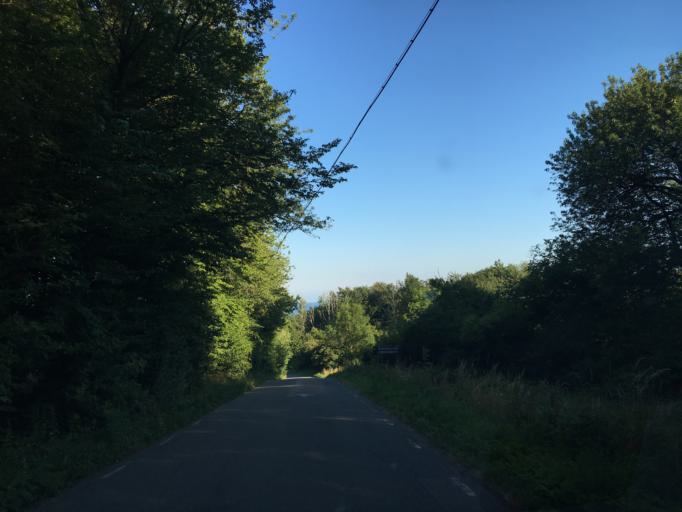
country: SE
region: Skane
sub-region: Simrishamns Kommun
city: Kivik
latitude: 55.6584
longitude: 14.2613
